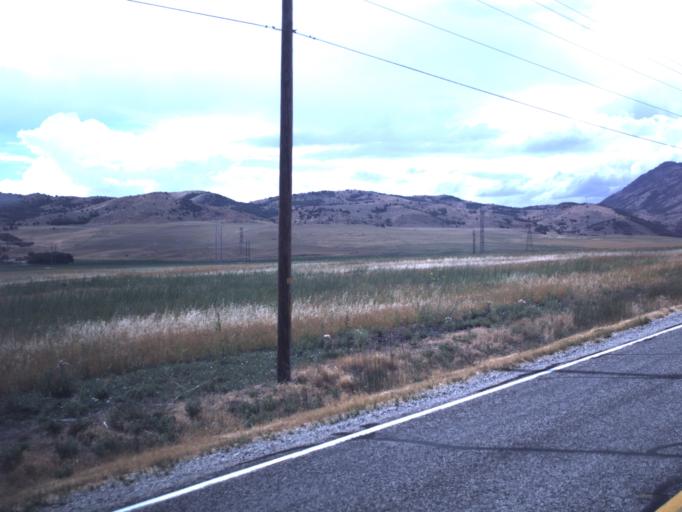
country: US
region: Utah
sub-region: Cache County
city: Benson
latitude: 41.8756
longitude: -112.0203
